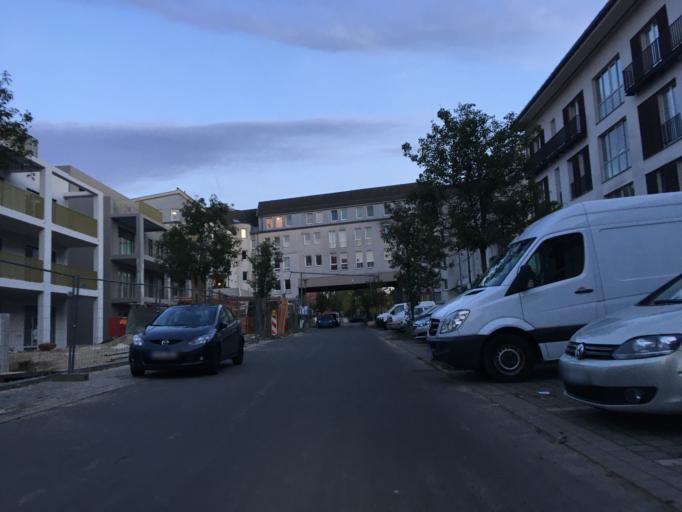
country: DE
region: Berlin
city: Buchholz
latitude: 52.6048
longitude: 13.4181
